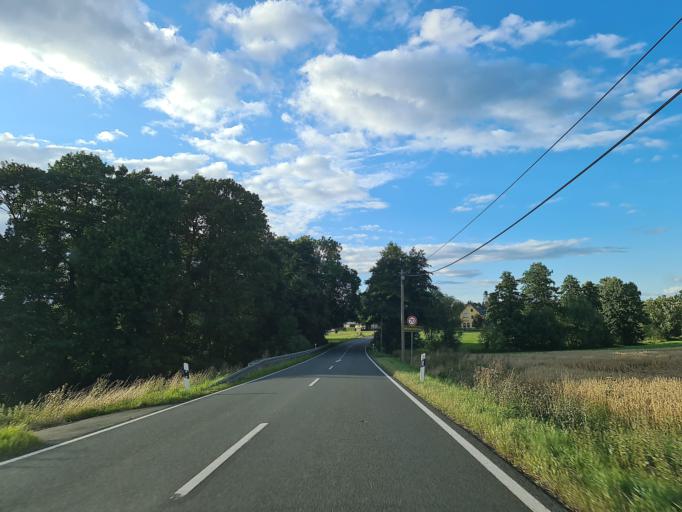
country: DE
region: Saxony
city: Pausa
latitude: 50.5968
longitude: 11.9966
